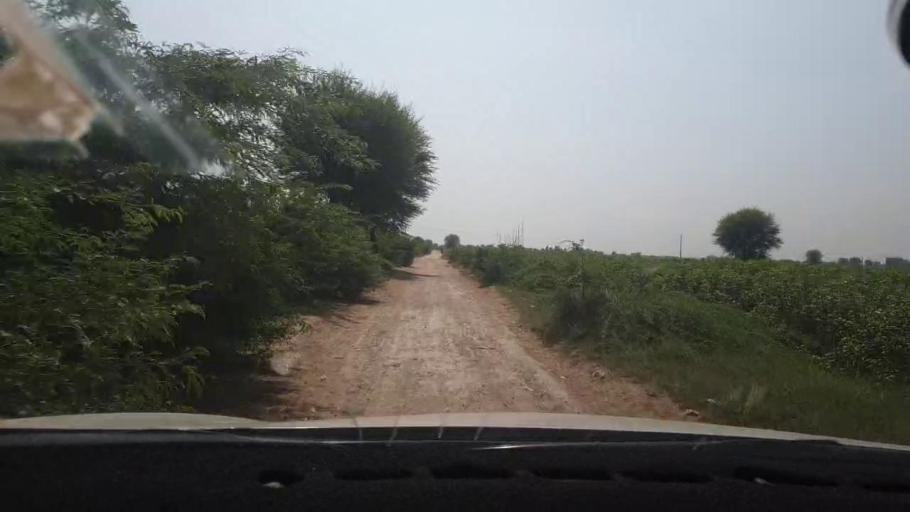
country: PK
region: Sindh
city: Tando Mittha Khan
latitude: 25.9326
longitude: 69.2247
